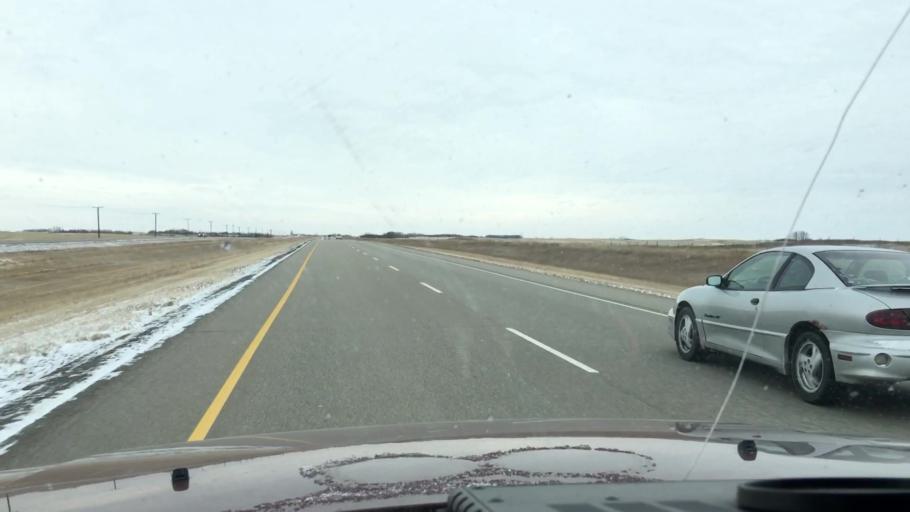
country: CA
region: Saskatchewan
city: Watrous
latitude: 51.4038
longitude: -106.1796
